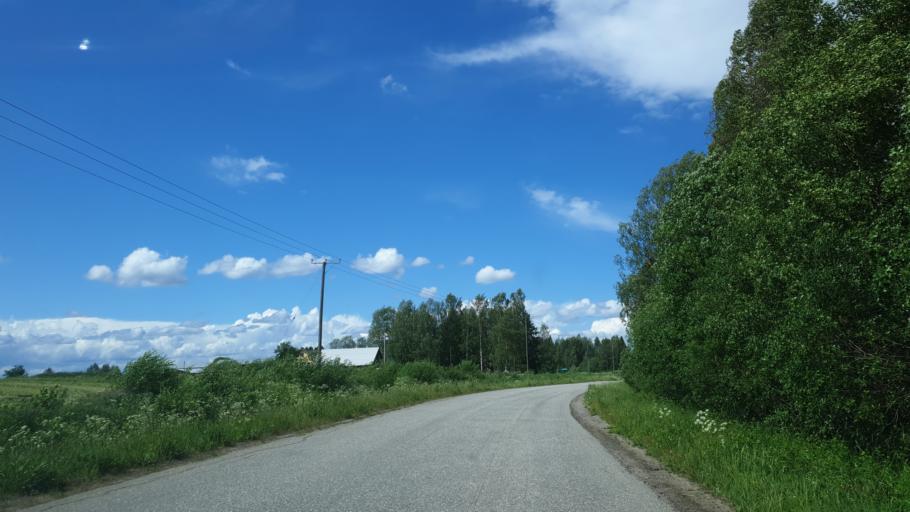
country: FI
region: Northern Savo
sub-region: Koillis-Savo
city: Kaavi
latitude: 62.9940
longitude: 28.7208
